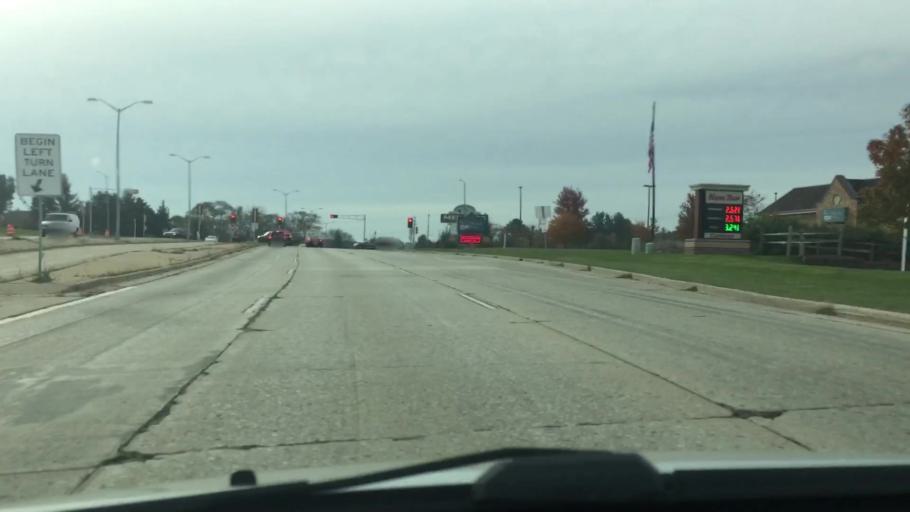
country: US
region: Wisconsin
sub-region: Milwaukee County
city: Hales Corners
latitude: 42.9256
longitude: -88.0479
